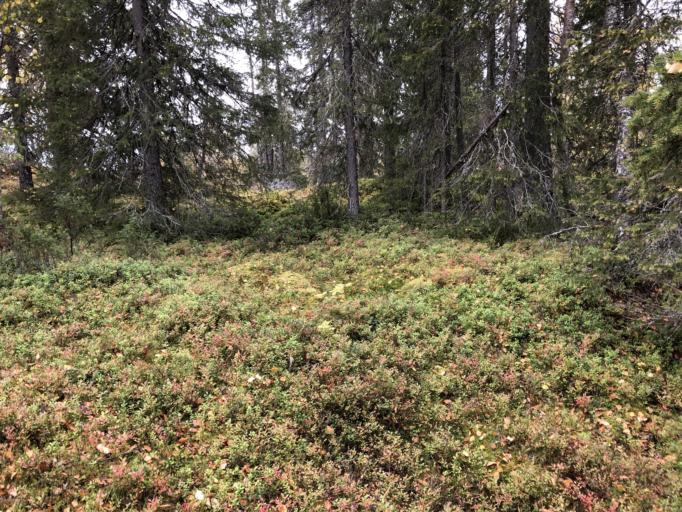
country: FI
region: Northern Ostrobothnia
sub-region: Koillismaa
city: Kuusamo
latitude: 66.5991
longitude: 29.3260
